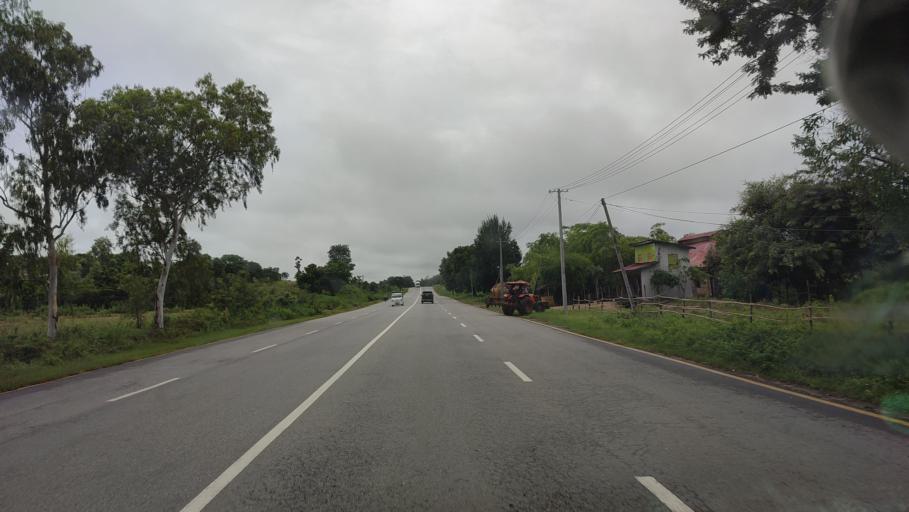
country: MM
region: Mandalay
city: Pyinmana
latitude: 19.9976
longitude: 96.2476
